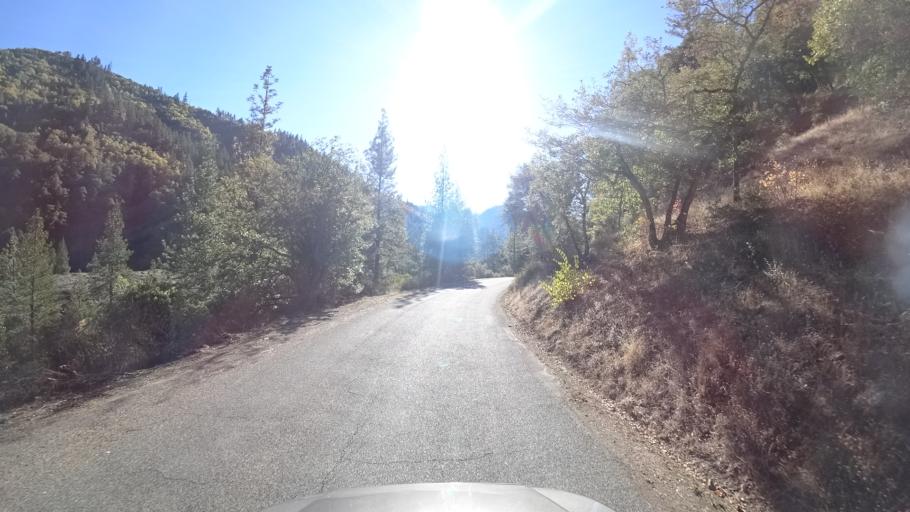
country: US
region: California
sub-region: Humboldt County
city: Willow Creek
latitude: 41.2670
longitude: -123.3062
